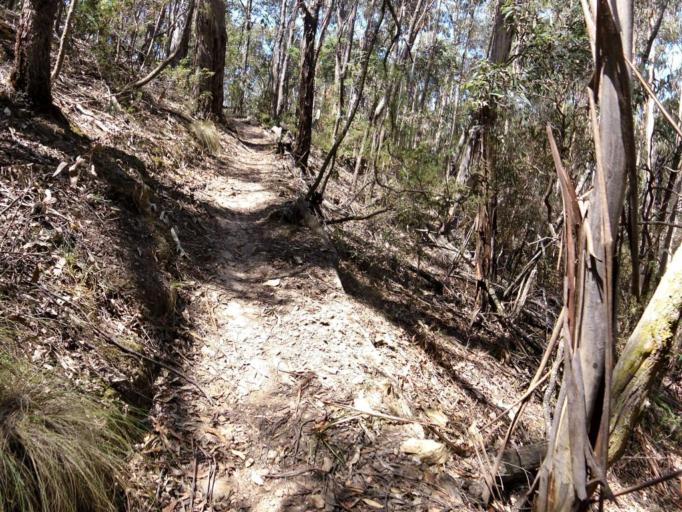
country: AU
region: Victoria
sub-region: Melton
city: Melton West
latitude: -37.4904
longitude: 144.5362
